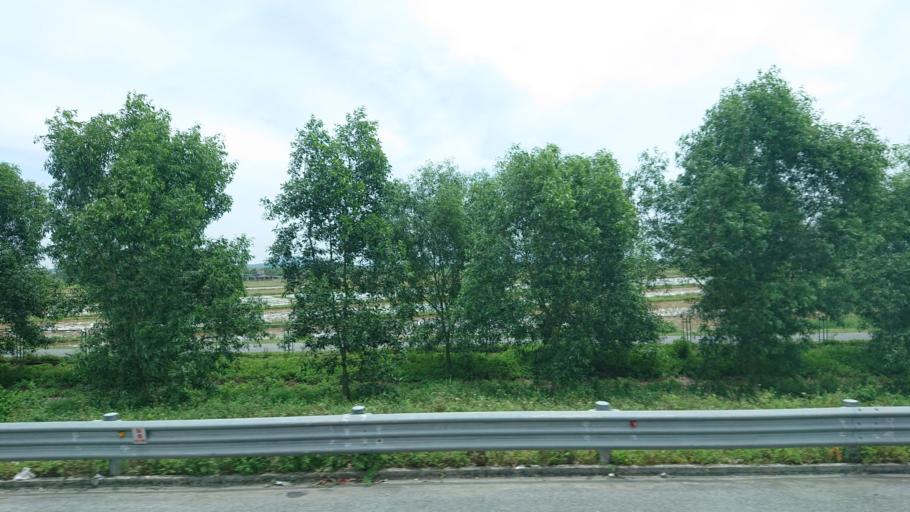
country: VN
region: Hai Phong
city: Nui Doi
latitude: 20.7659
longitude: 106.6516
